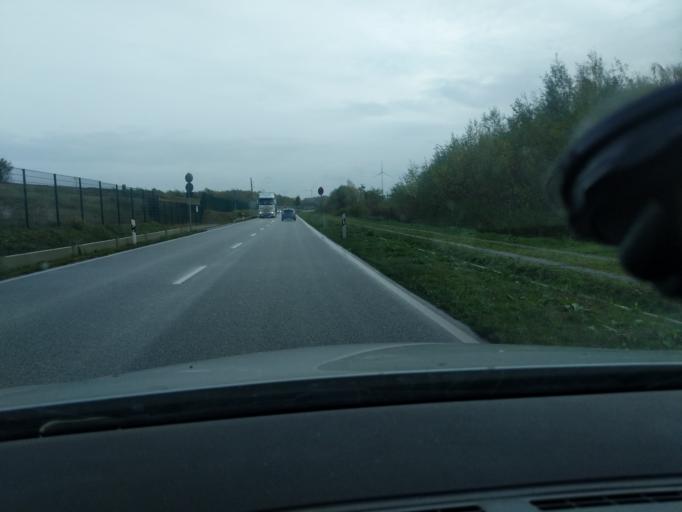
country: DE
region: Lower Saxony
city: Neu Wulmstorf
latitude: 53.5120
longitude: 9.8581
